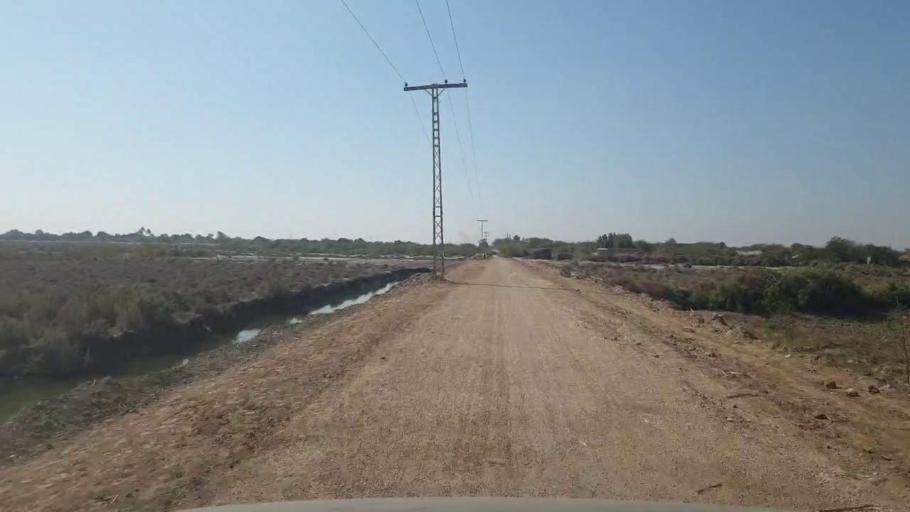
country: PK
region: Sindh
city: Mirwah Gorchani
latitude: 25.2659
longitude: 69.1071
